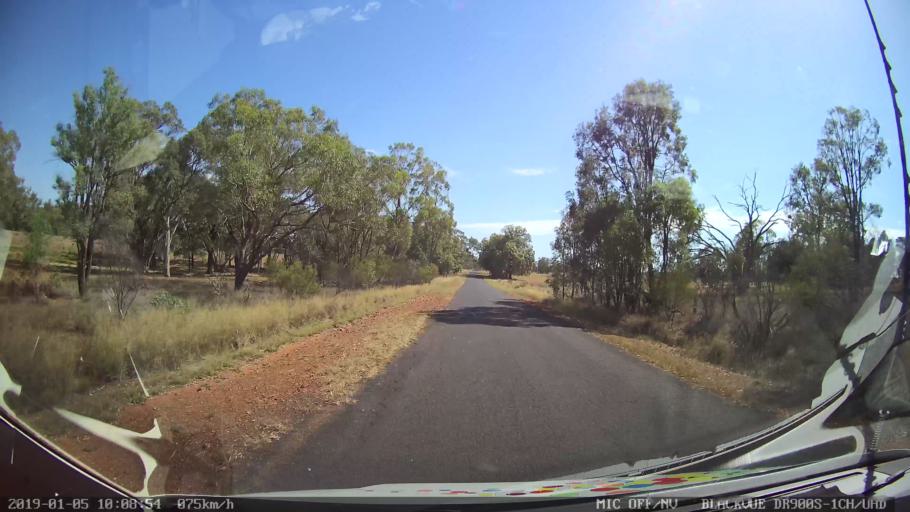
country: AU
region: New South Wales
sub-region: Gilgandra
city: Gilgandra
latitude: -31.6365
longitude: 148.8830
